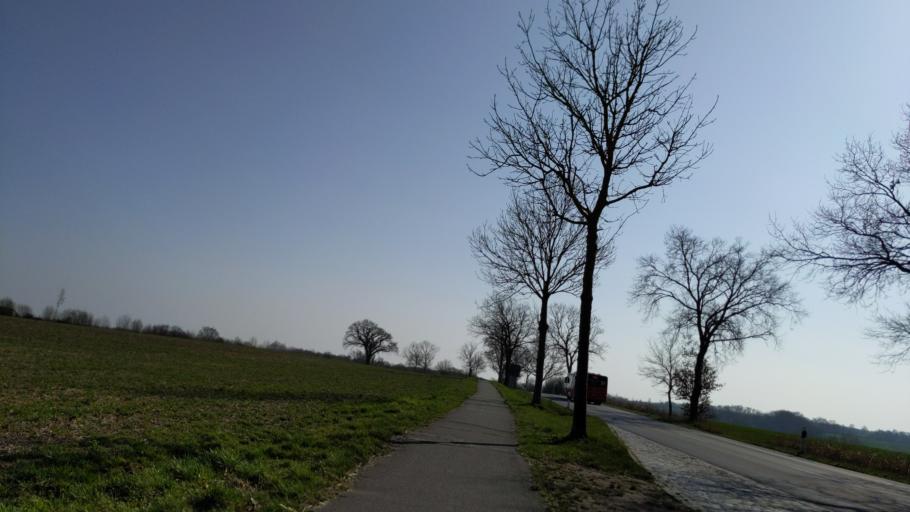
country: DE
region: Schleswig-Holstein
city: Altenkrempe
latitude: 54.1311
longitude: 10.8480
